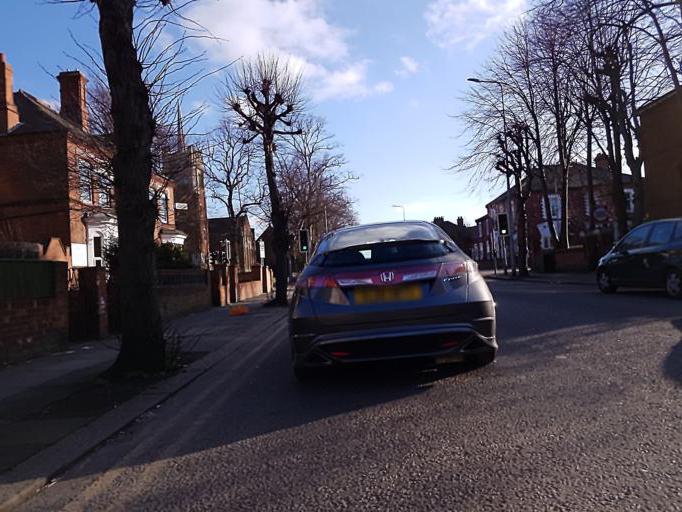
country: GB
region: England
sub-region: North East Lincolnshire
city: Grimsby
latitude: 53.5596
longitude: -0.0766
